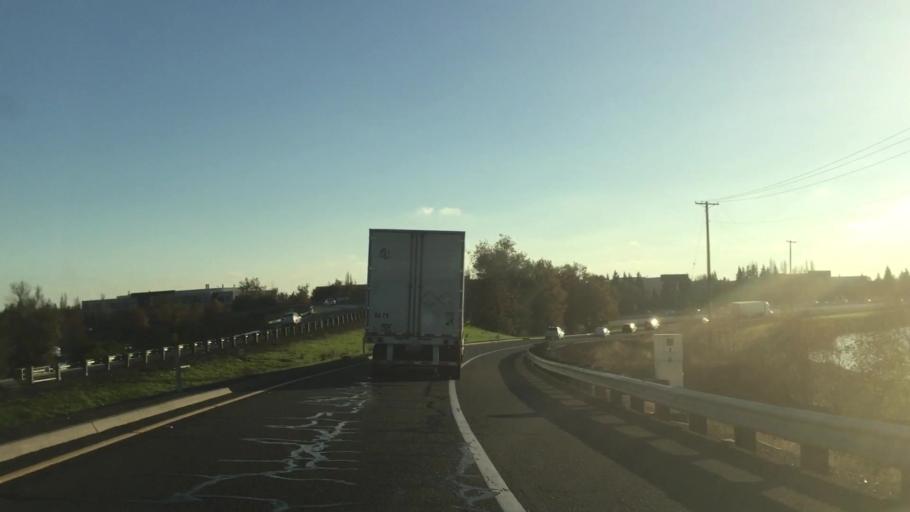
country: US
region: California
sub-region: Yolo County
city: West Sacramento
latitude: 38.6259
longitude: -121.5186
